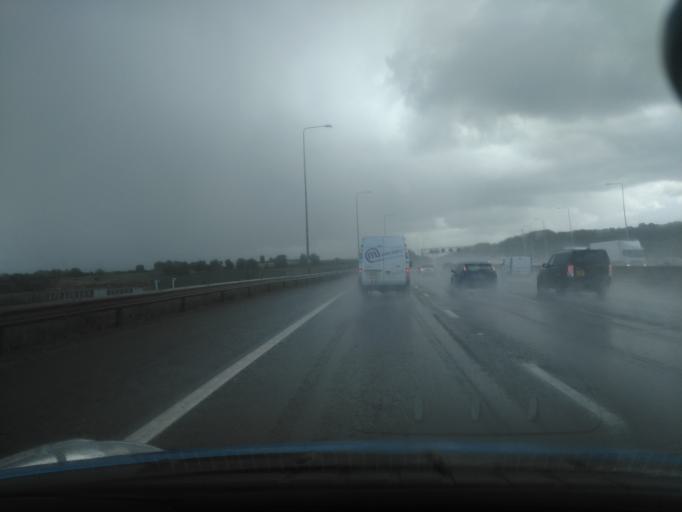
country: GB
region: England
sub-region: Hertfordshire
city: Shenley AV
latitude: 51.7140
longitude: -0.2668
